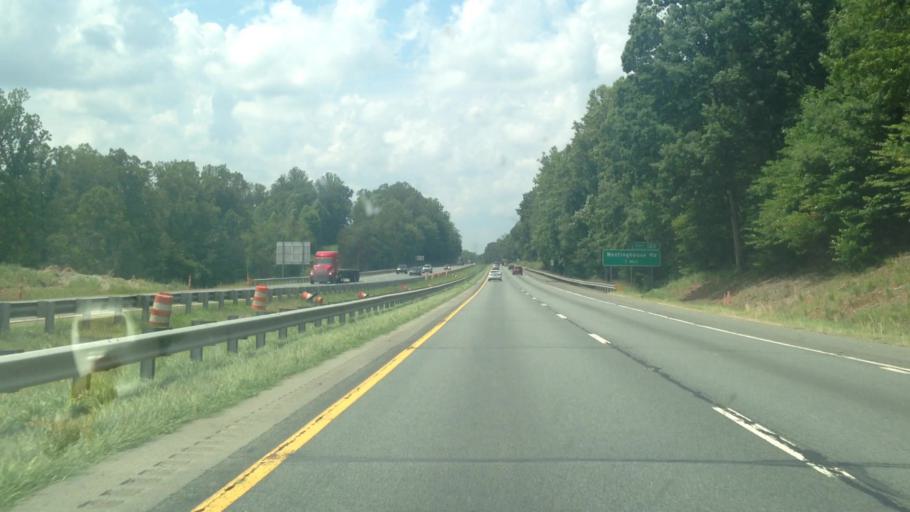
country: US
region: North Carolina
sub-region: Forsyth County
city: Rural Hall
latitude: 36.2143
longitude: -80.3065
